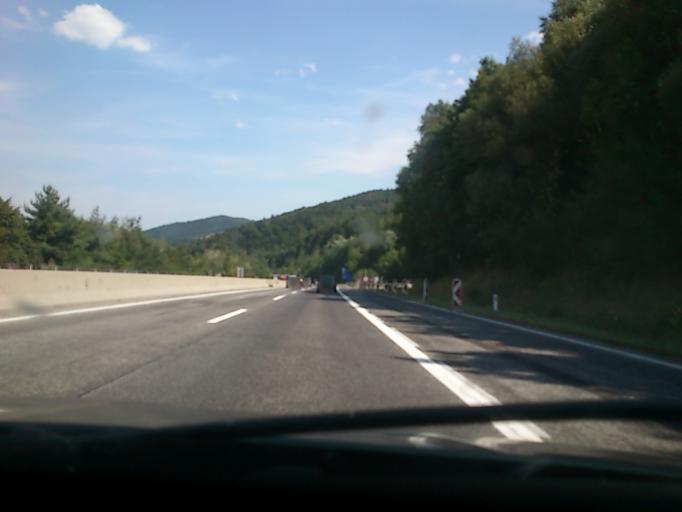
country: AT
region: Lower Austria
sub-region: Politischer Bezirk Neunkirchen
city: Grimmenstein
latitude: 47.6195
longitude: 16.1319
